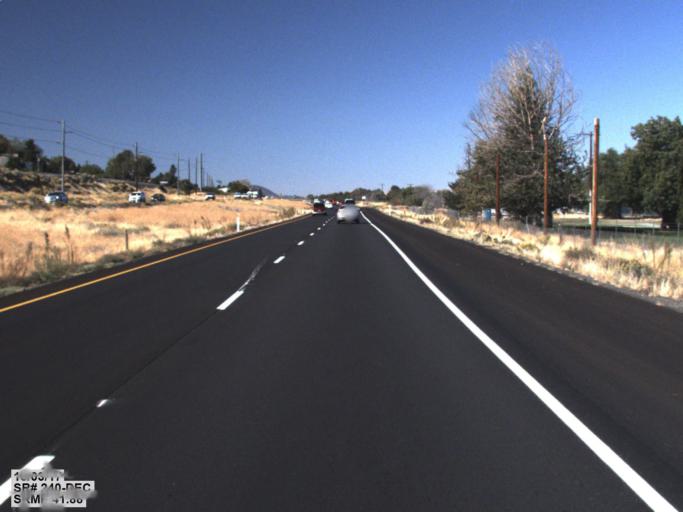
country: US
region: Washington
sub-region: Benton County
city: Kennewick
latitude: 46.2230
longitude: -119.1631
